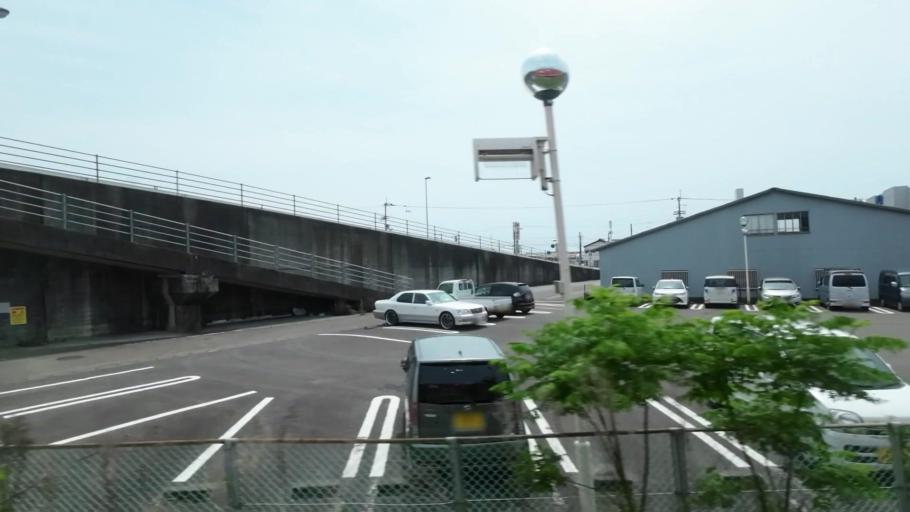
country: JP
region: Kochi
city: Kochi-shi
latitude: 33.6028
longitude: 133.6753
